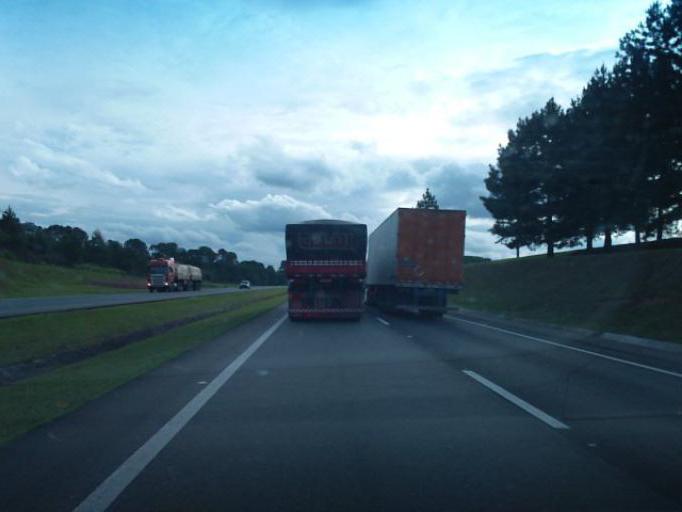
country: BR
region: Parana
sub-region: Piraquara
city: Piraquara
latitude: -25.4143
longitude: -49.0669
